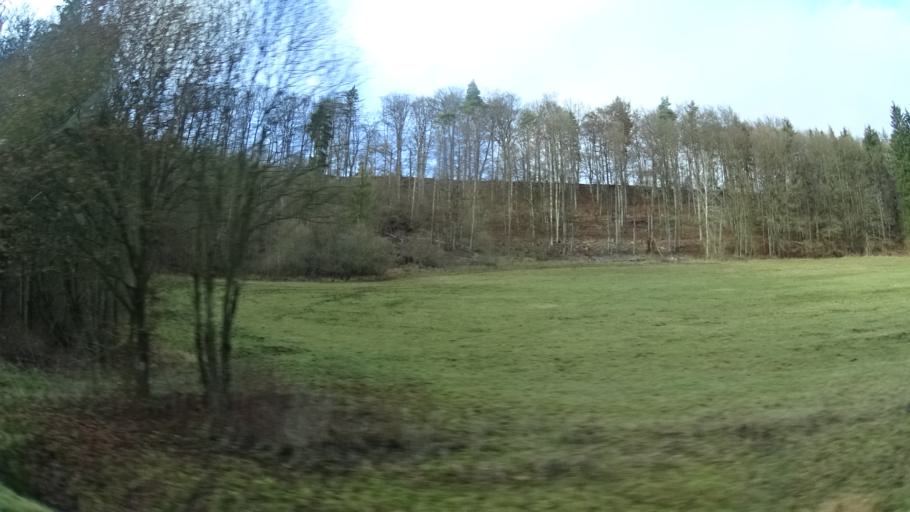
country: DE
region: Thuringia
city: Utendorf
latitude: 50.5965
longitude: 10.4417
